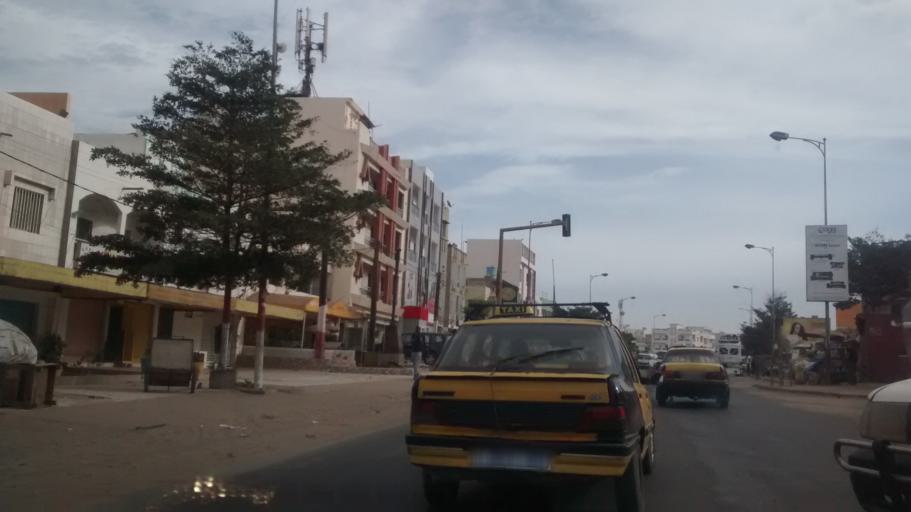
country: SN
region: Dakar
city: Grand Dakar
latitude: 14.7492
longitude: -17.4432
